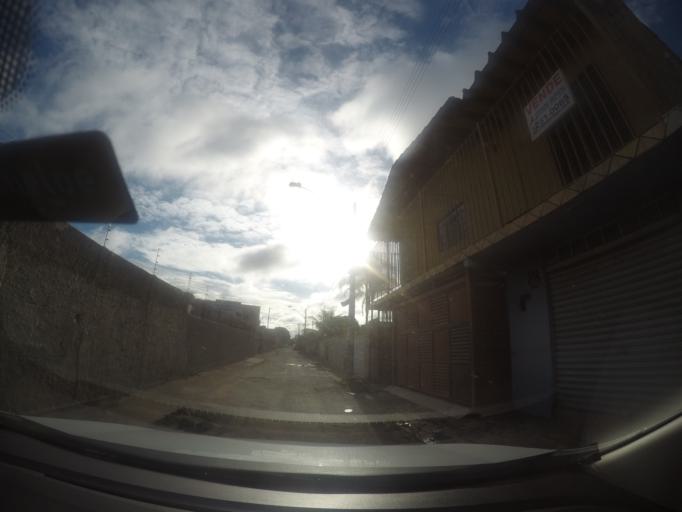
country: BR
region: Goias
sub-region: Goiania
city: Goiania
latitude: -16.6885
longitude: -49.3147
